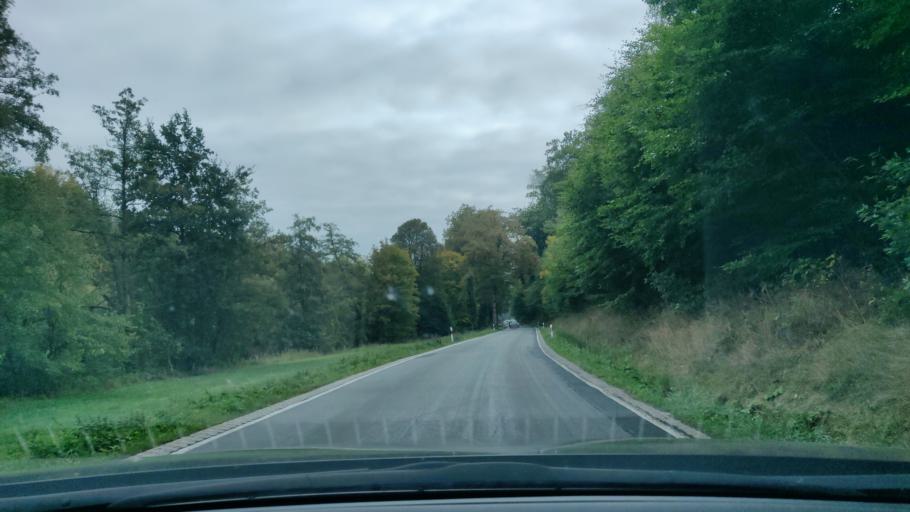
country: DE
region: Hesse
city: Schwalmstadt
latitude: 50.9622
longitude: 9.2036
